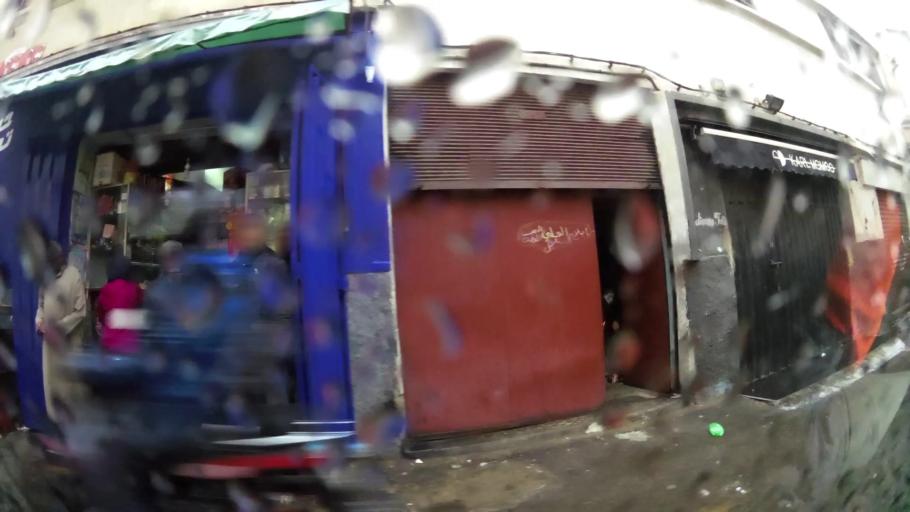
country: MA
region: Grand Casablanca
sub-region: Casablanca
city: Casablanca
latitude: 33.5718
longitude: -7.6071
